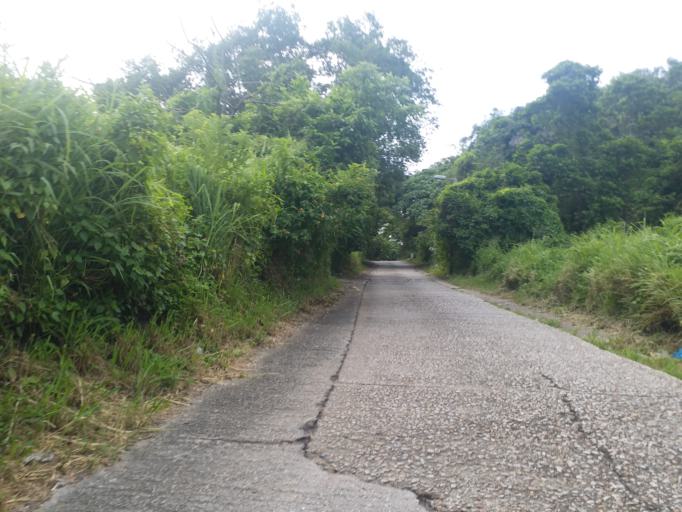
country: HK
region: Yuen Long
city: Yuen Long Kau Hui
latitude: 22.4373
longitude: 114.0014
